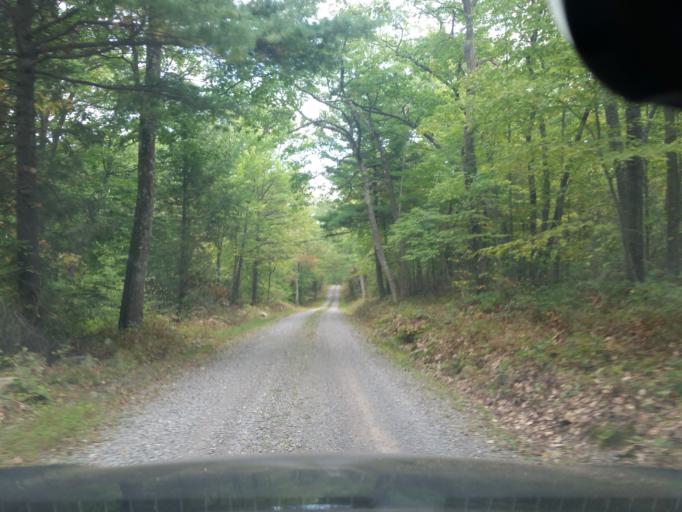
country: US
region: Pennsylvania
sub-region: Lycoming County
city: Jersey Shore
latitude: 41.0872
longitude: -77.1864
